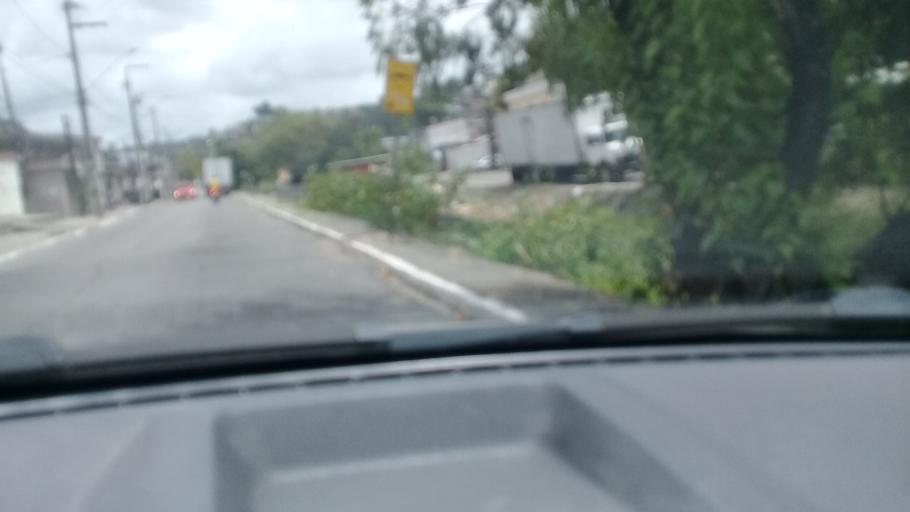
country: BR
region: Pernambuco
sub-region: Jaboatao Dos Guararapes
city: Jaboatao dos Guararapes
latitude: -8.1233
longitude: -34.9505
